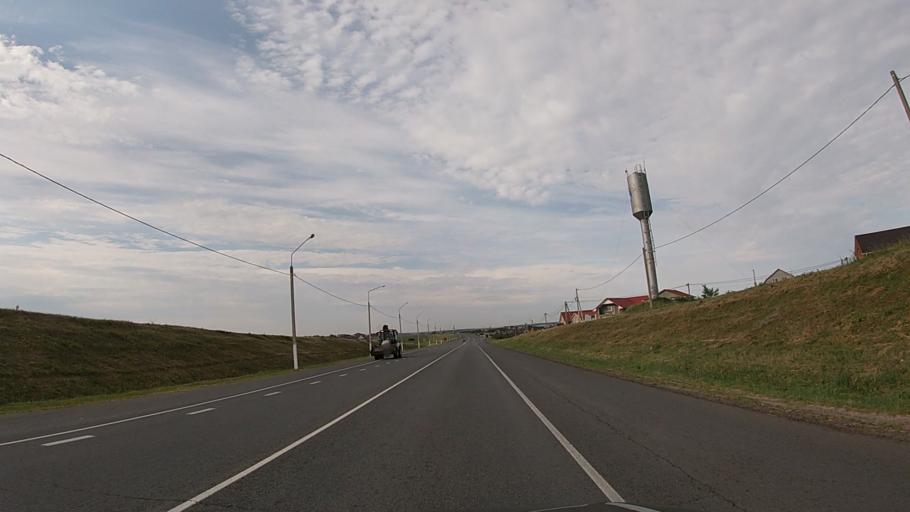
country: RU
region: Belgorod
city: Severnyy
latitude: 50.6628
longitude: 36.4690
